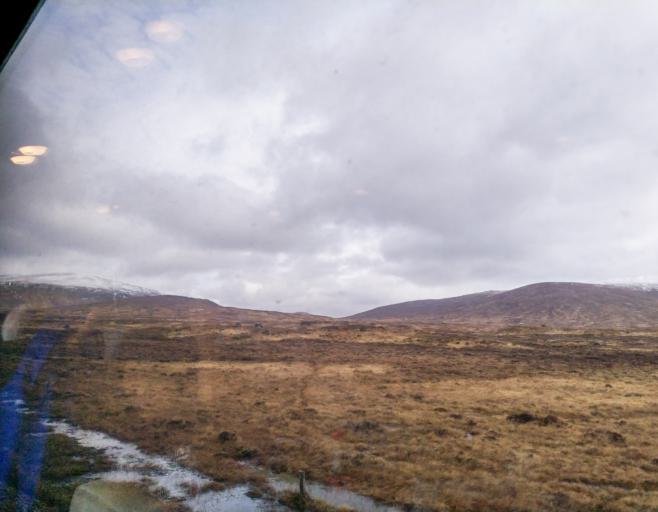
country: GB
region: Scotland
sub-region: Highland
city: Spean Bridge
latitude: 56.7345
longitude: -4.6537
